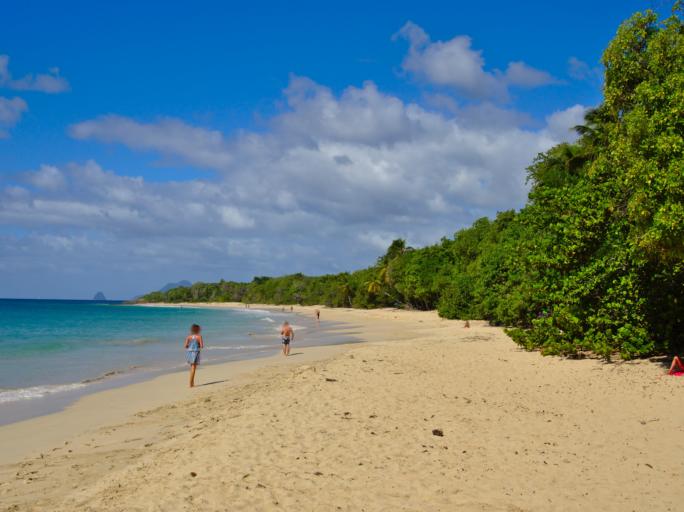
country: MQ
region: Martinique
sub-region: Martinique
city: Le Marin
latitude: 14.4037
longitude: -60.8793
